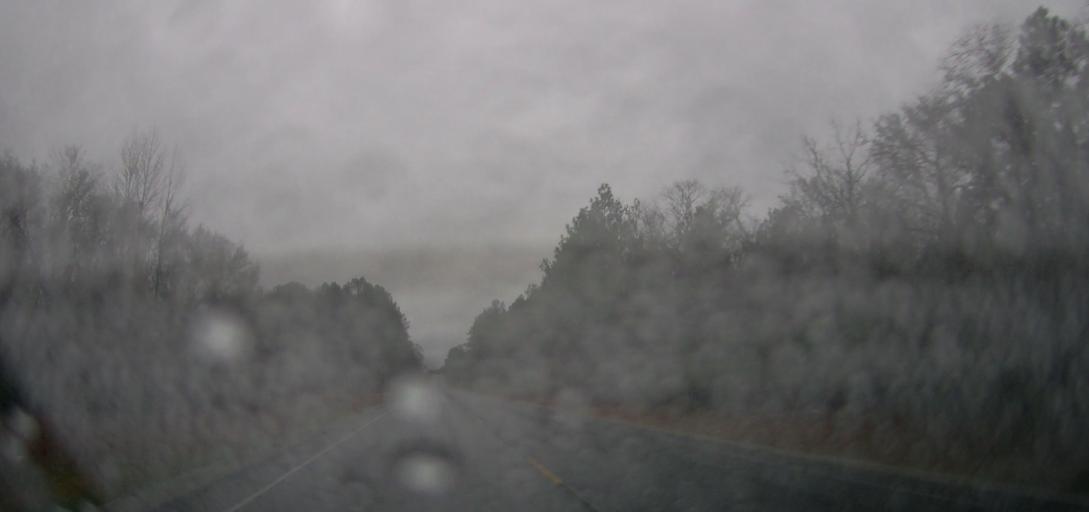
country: US
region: Alabama
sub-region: Autauga County
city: Pine Level
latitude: 32.6009
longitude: -86.7109
